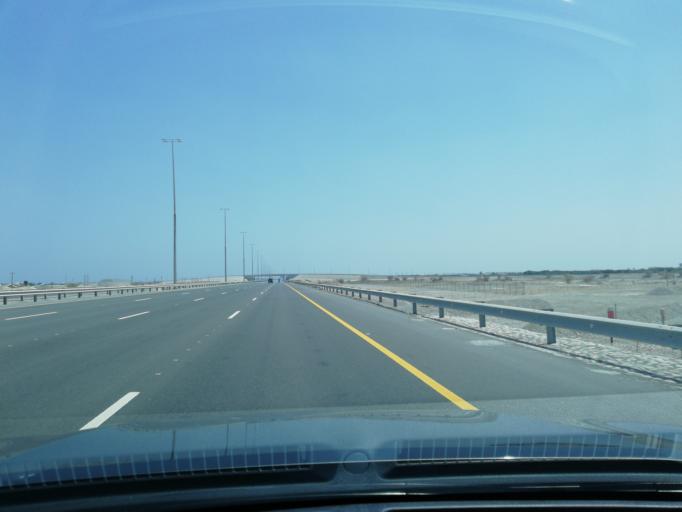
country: OM
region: Al Batinah
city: Barka'
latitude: 23.6176
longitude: 57.8376
